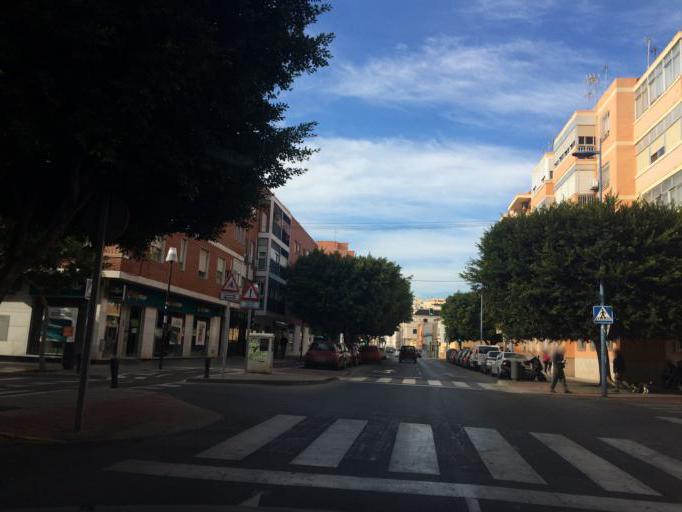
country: ES
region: Andalusia
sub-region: Provincia de Almeria
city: Almeria
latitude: 36.8434
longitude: -2.4491
